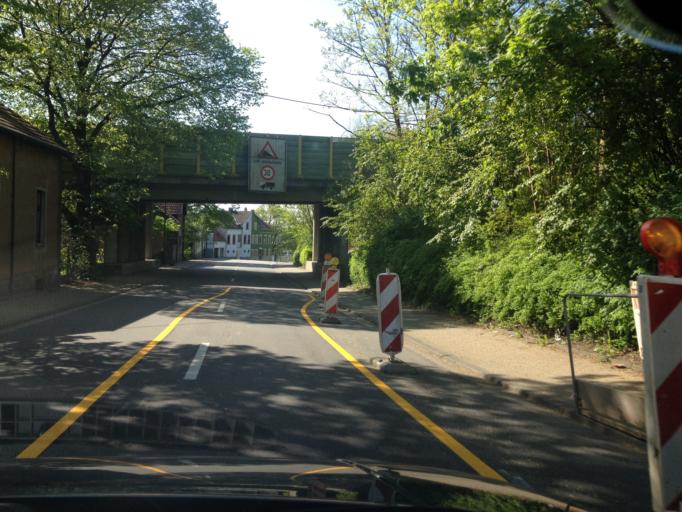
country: DE
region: Saarland
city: Sulzbach
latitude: 49.3050
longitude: 7.0573
